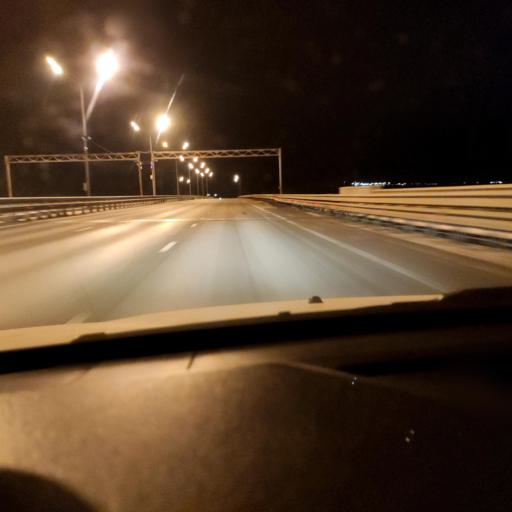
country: RU
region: Samara
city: Smyshlyayevka
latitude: 53.1782
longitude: 50.3084
